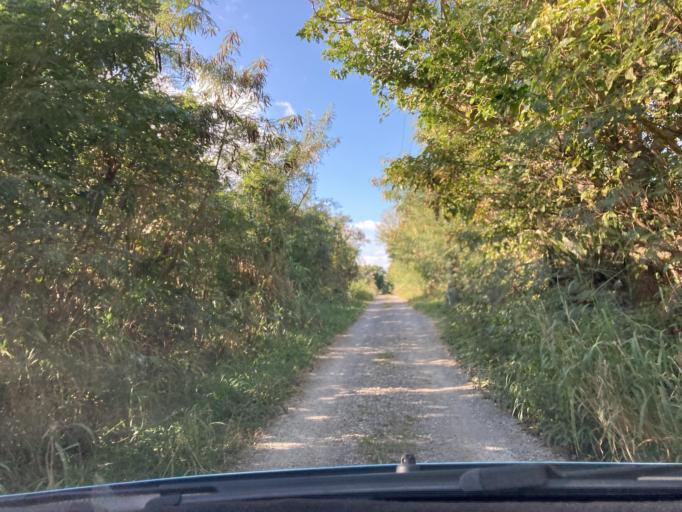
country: JP
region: Okinawa
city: Katsuren-haebaru
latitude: 26.3169
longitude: 127.9276
